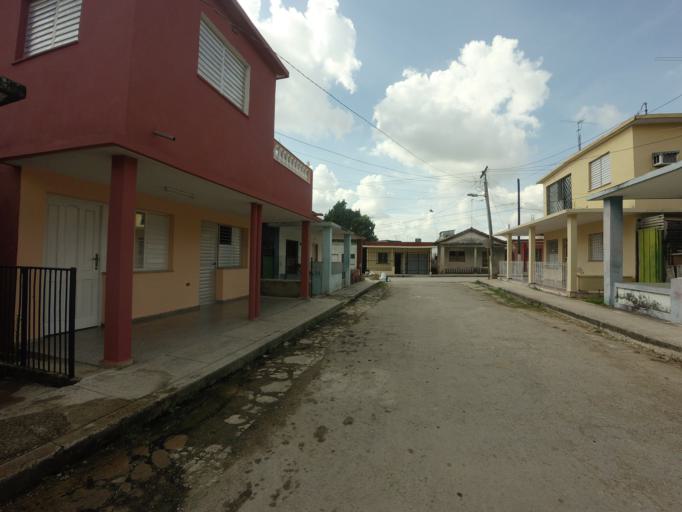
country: CU
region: Artemisa
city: Bauta
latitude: 22.9862
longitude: -82.5476
